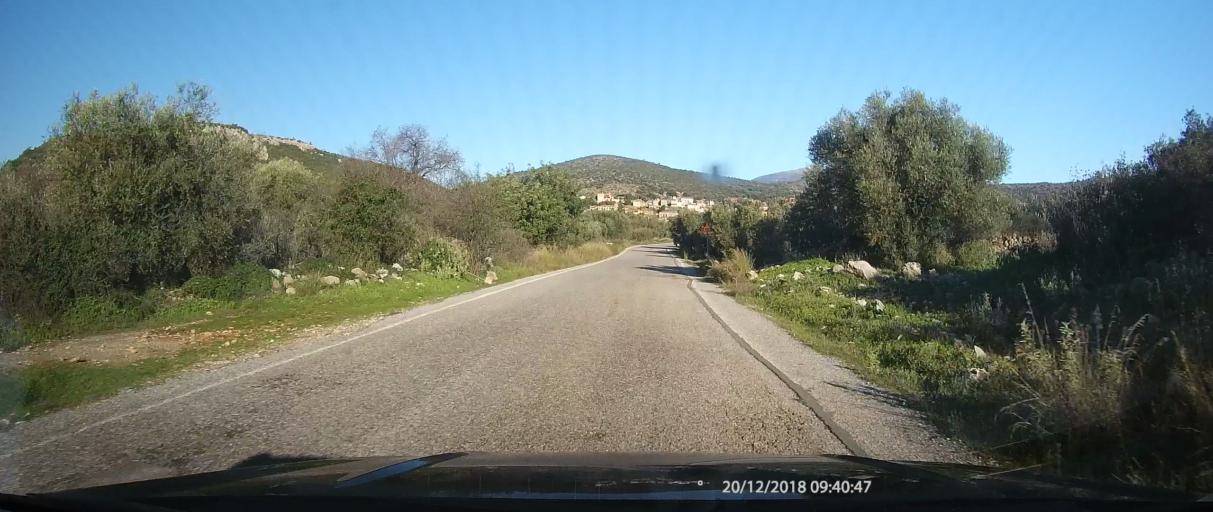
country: GR
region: Peloponnese
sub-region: Nomos Lakonias
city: Yerakion
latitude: 36.9476
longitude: 22.7669
